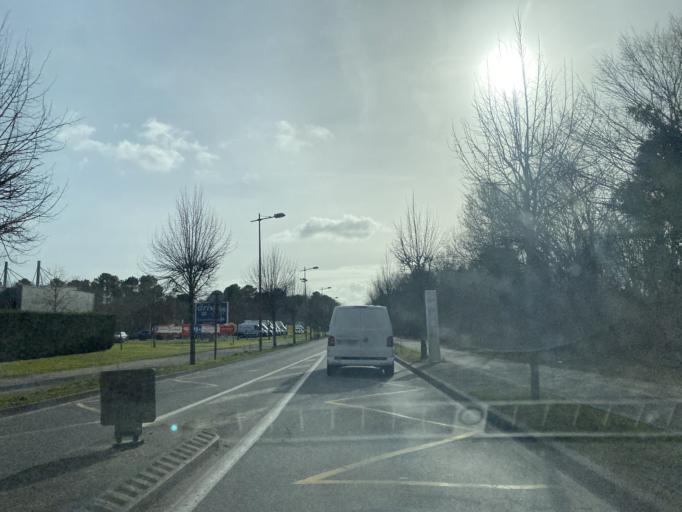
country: FR
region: Aquitaine
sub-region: Departement de la Gironde
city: Le Taillan-Medoc
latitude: 44.9138
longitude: -0.6686
